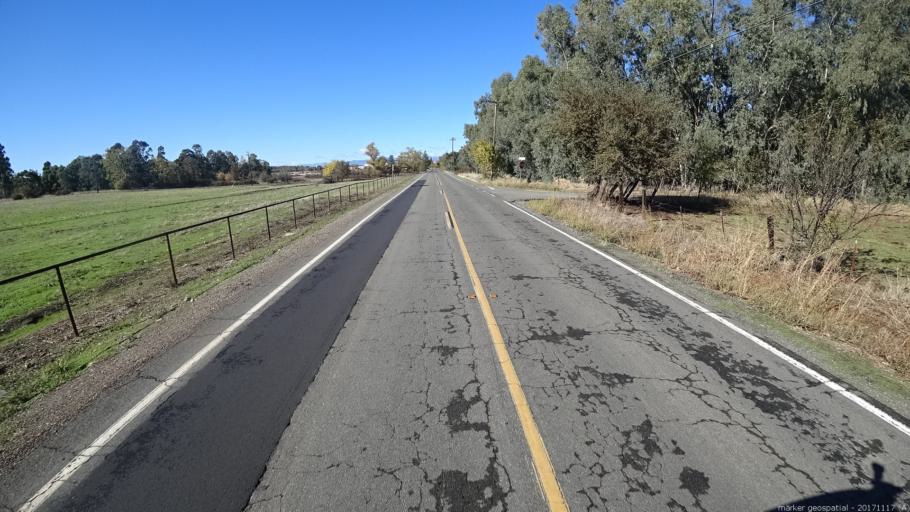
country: US
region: California
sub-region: Shasta County
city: Anderson
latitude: 40.4317
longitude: -122.2574
